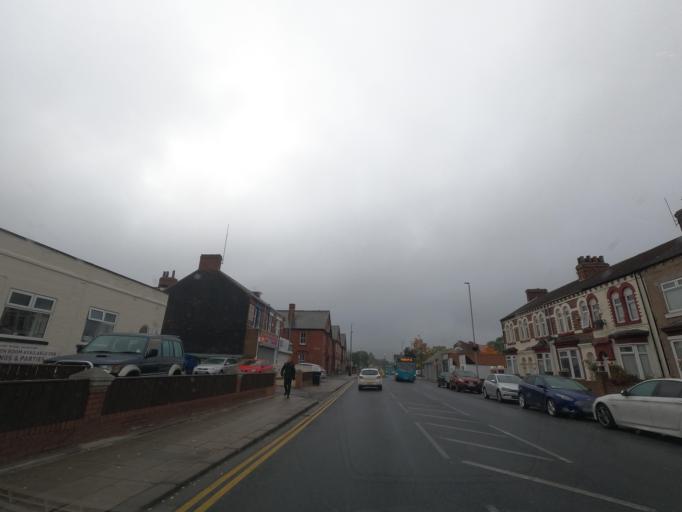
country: GB
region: England
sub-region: Middlesbrough
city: Middlesbrough
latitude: 54.5699
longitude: -1.2121
